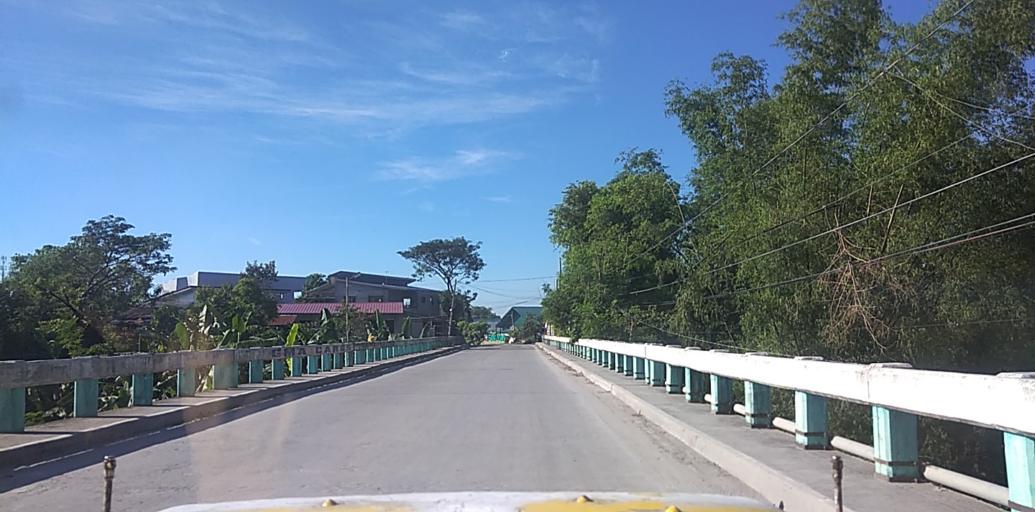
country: PH
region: Central Luzon
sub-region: Province of Pampanga
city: Anao
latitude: 15.1185
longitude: 120.7030
